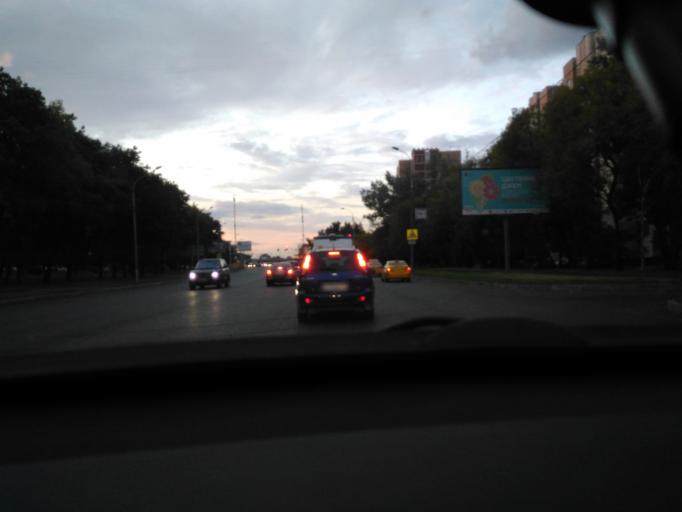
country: RU
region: Moscow
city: Vatutino
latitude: 55.8900
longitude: 37.6744
